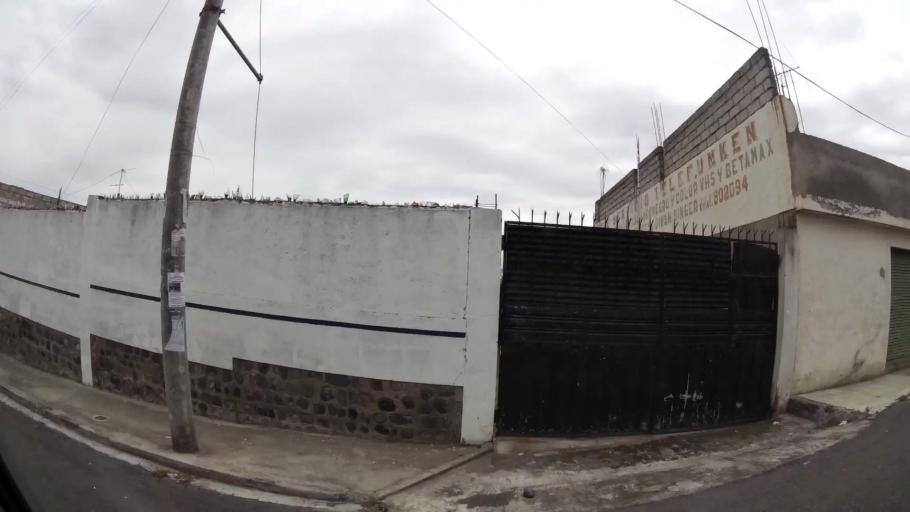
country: EC
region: Cotopaxi
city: Latacunga
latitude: -0.9576
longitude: -78.6128
